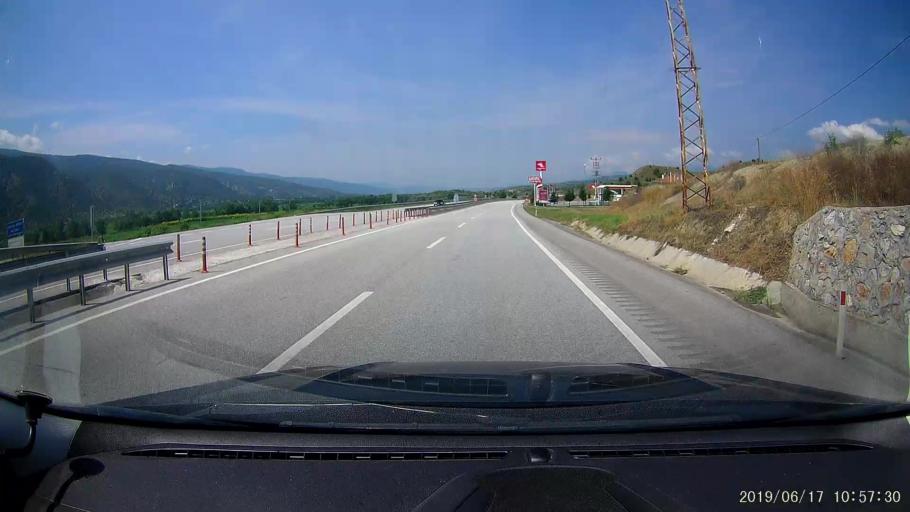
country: TR
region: Corum
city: Hacihamza
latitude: 41.0487
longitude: 34.2455
